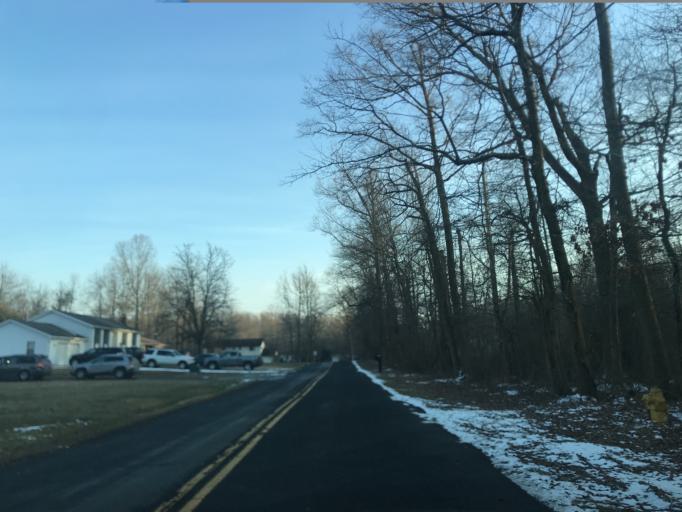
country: US
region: Maryland
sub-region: Harford County
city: Riverside
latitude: 39.4370
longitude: -76.2558
